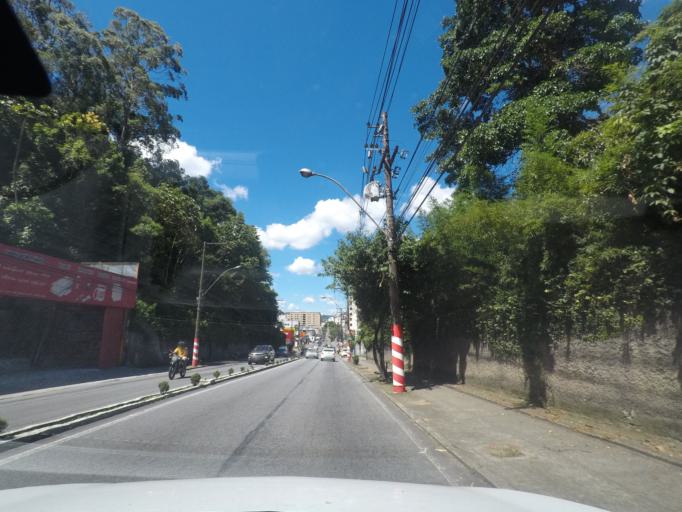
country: BR
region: Rio de Janeiro
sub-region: Teresopolis
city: Teresopolis
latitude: -22.4244
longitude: -42.9785
